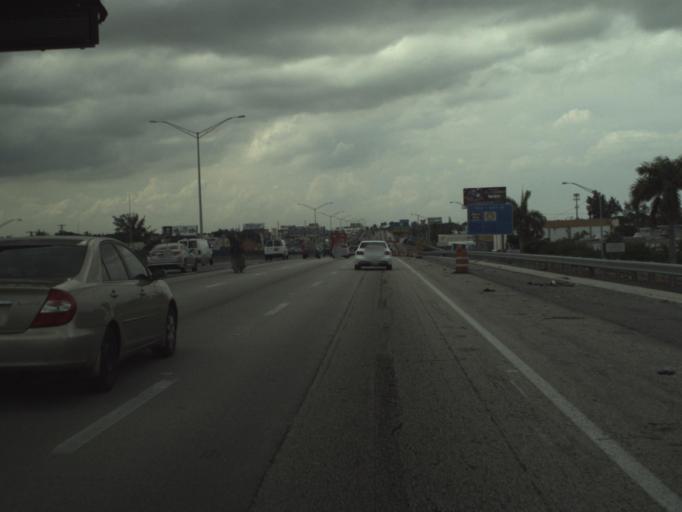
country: US
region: Florida
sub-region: Broward County
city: Pembroke Park
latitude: 25.9857
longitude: -80.1655
